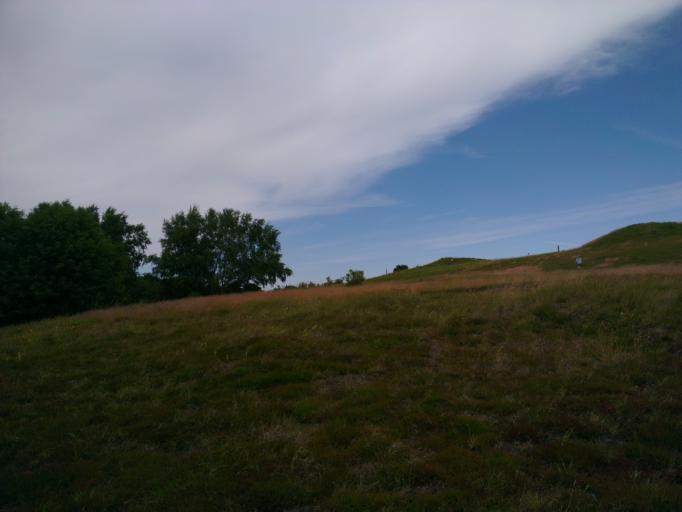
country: DK
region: Capital Region
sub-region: Frederikssund Kommune
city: Jaegerspris
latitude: 55.8958
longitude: 11.9299
